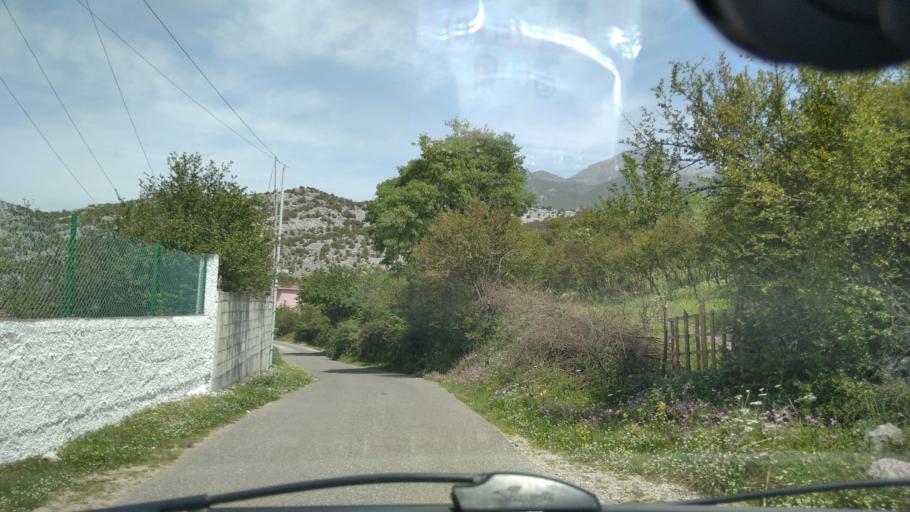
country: AL
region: Shkoder
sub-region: Rrethi i Malesia e Madhe
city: Gruemire
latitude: 42.1419
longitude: 19.5477
